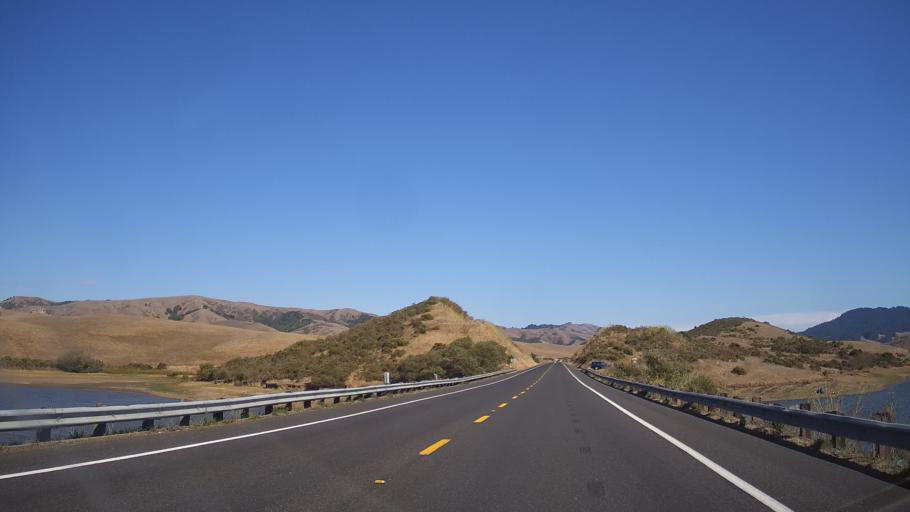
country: US
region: California
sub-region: Marin County
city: Lagunitas-Forest Knolls
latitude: 38.0922
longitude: -122.7465
